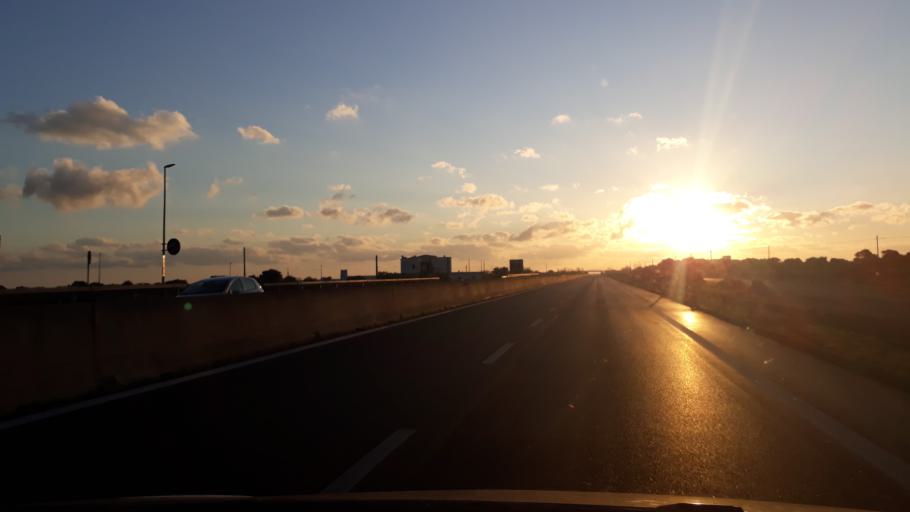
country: IT
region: Apulia
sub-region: Provincia di Brindisi
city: Ostuni
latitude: 40.7771
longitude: 17.6051
